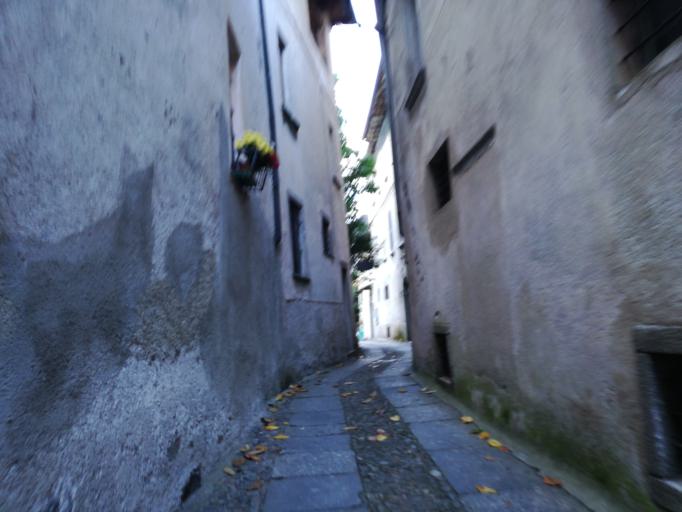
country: IT
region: Piedmont
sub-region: Provincia di Novara
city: Orta San Giulio
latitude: 45.7954
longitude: 8.3999
